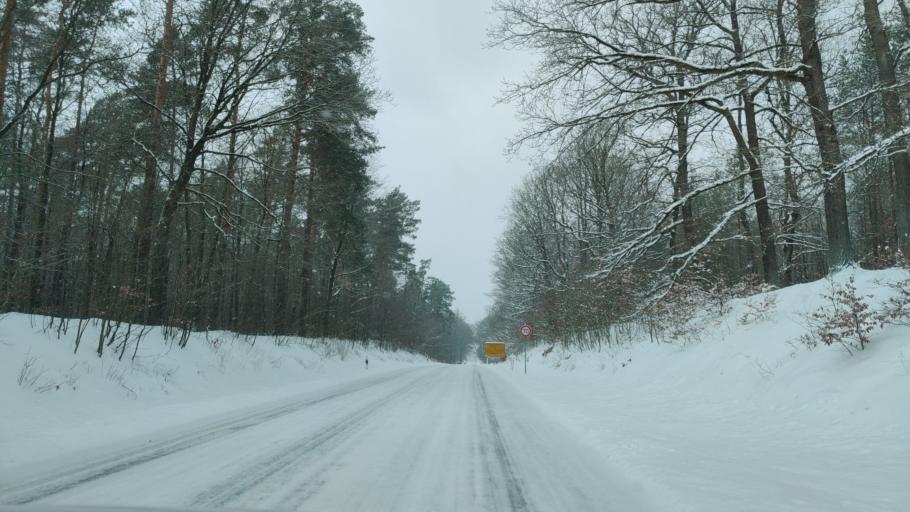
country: DE
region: Saxony
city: Bad Duben
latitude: 51.6543
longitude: 12.5964
